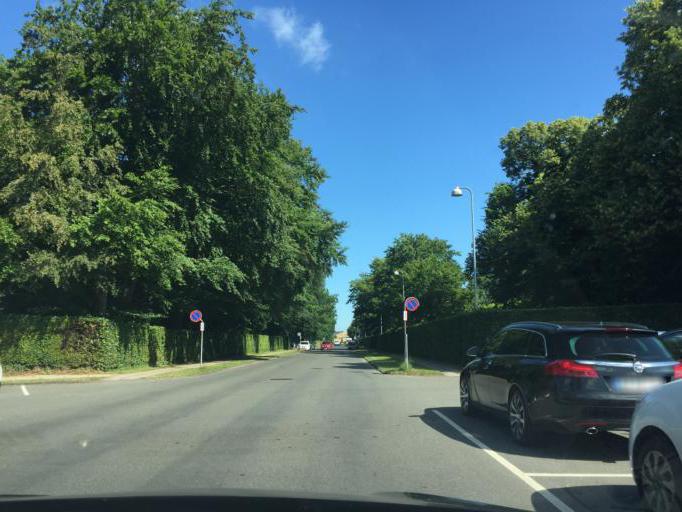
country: DK
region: South Denmark
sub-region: Odense Kommune
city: Odense
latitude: 55.3869
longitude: 10.3692
